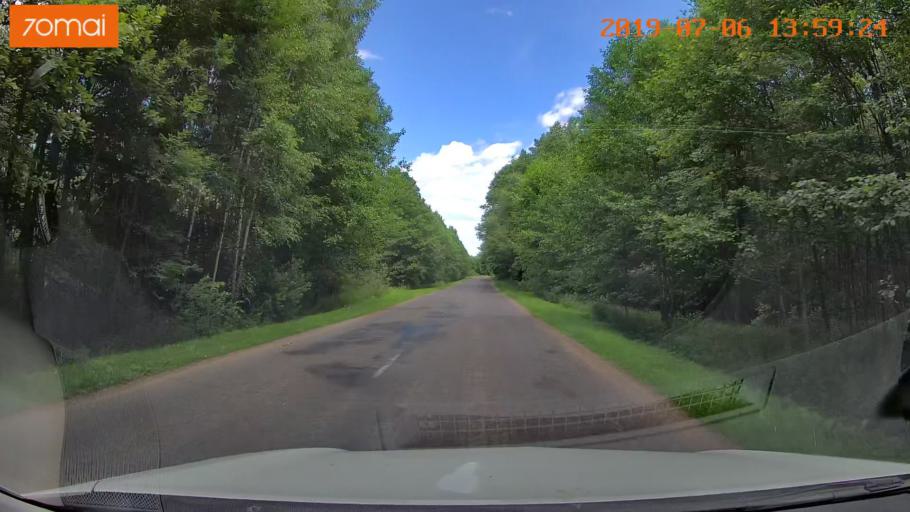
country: BY
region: Minsk
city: Ivyanyets
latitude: 53.7942
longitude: 26.8136
